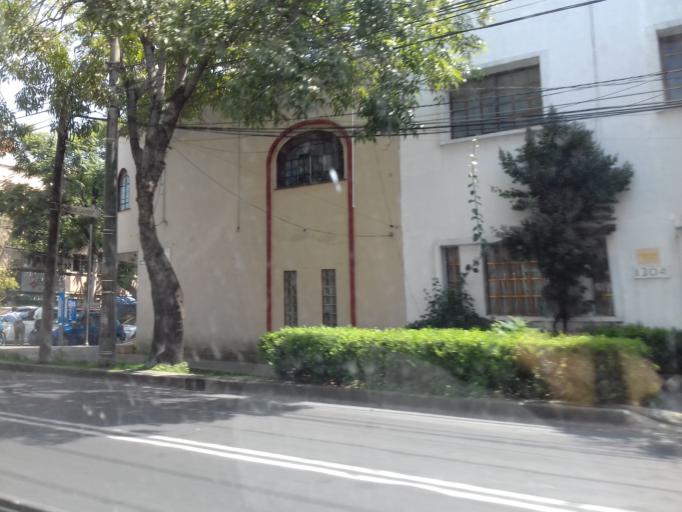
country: MX
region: Mexico City
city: Colonia del Valle
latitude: 19.3753
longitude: -99.1669
